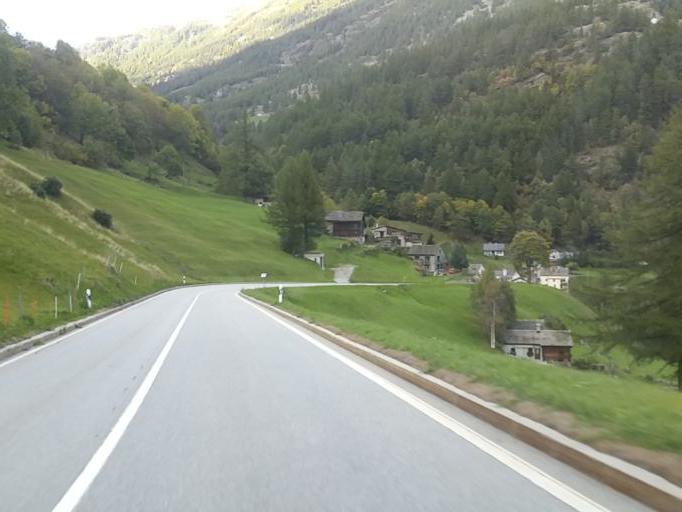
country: IT
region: Piedmont
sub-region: Provincia Verbano-Cusio-Ossola
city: Antronapiana
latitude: 46.1813
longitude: 8.0728
